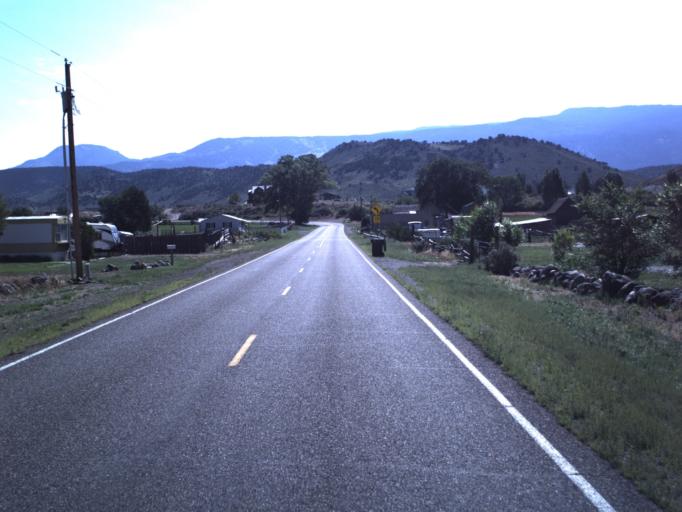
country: US
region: Utah
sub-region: Wayne County
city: Loa
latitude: 38.4622
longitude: -111.5999
